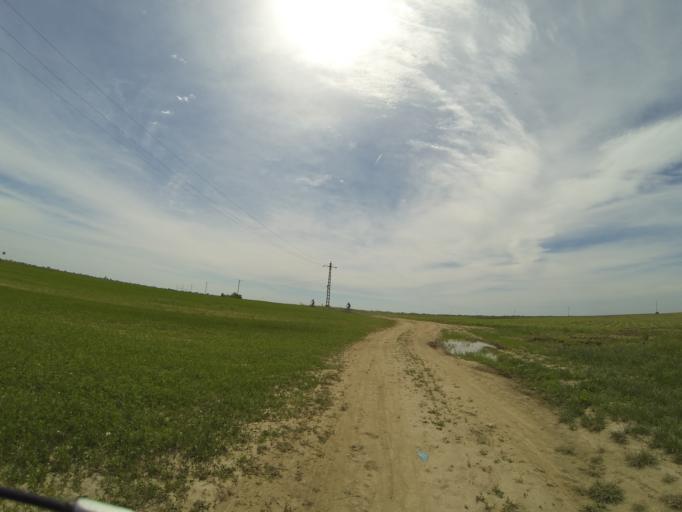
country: RO
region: Dolj
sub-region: Comuna Ghindeni
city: Ghindeni
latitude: 44.2061
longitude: 23.9580
